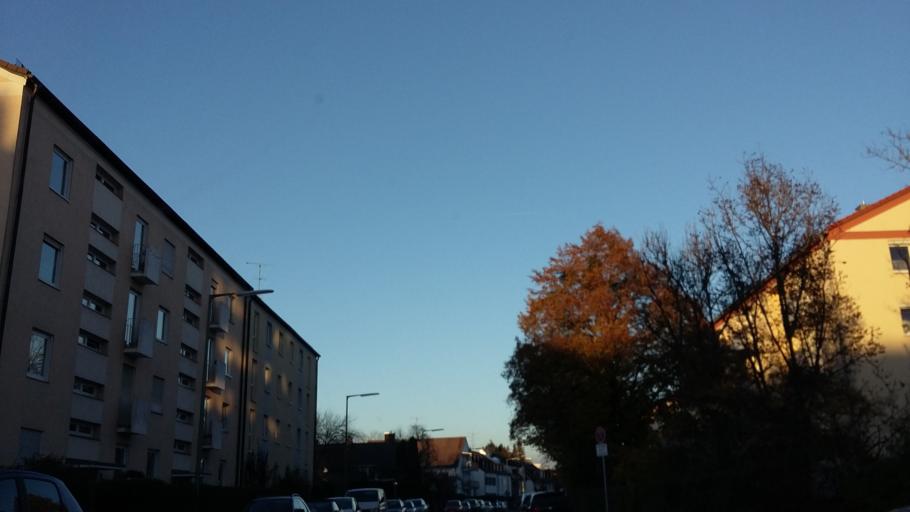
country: DE
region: Bavaria
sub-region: Upper Bavaria
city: Pasing
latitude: 48.1294
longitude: 11.4950
